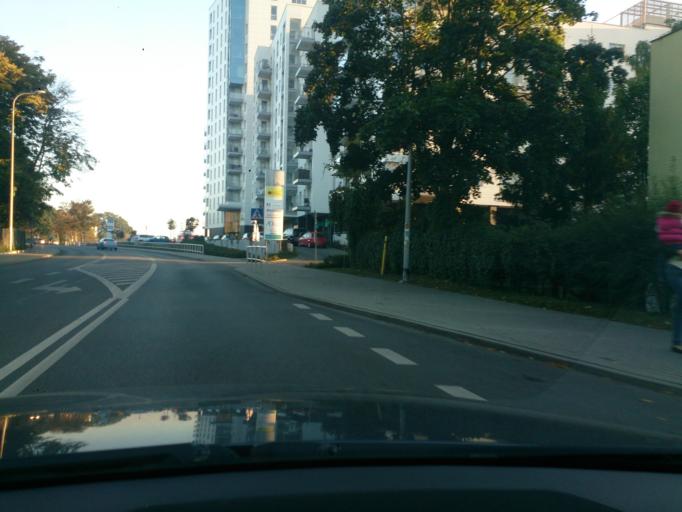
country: PL
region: Pomeranian Voivodeship
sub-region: Gdynia
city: Gdynia
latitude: 54.4923
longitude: 18.5422
